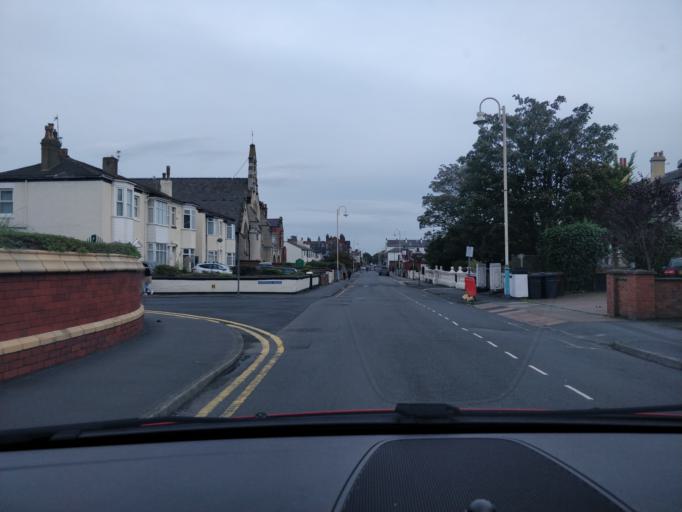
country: GB
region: England
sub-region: Sefton
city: Southport
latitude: 53.6529
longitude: -3.0033
